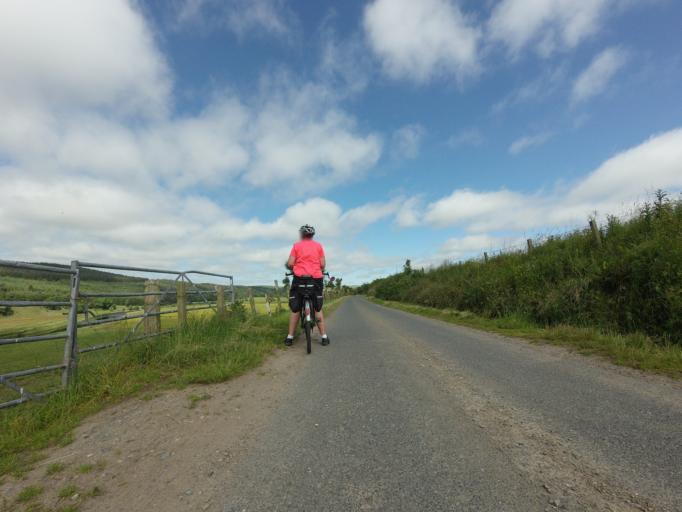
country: GB
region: Scotland
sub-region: Aberdeenshire
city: Turriff
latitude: 57.5707
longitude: -2.4991
